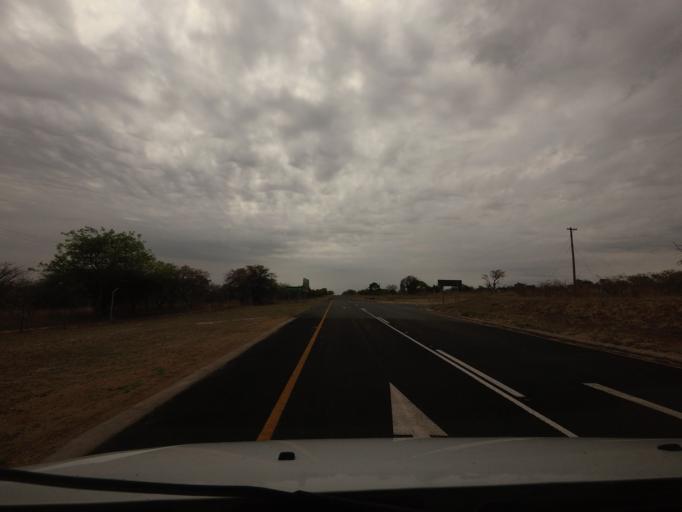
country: ZA
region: Limpopo
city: Thulamahashi
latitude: -24.5627
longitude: 31.1445
